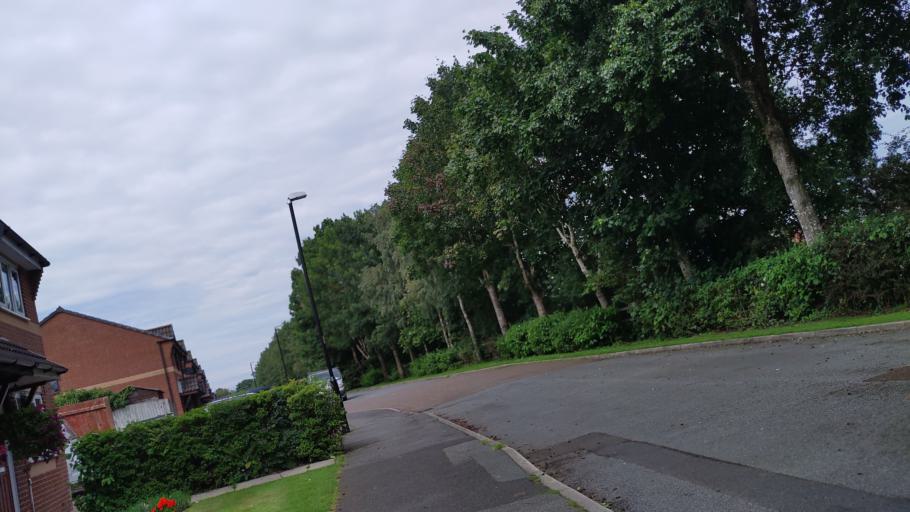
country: GB
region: England
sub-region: Lancashire
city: Chorley
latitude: 53.6524
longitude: -2.6140
